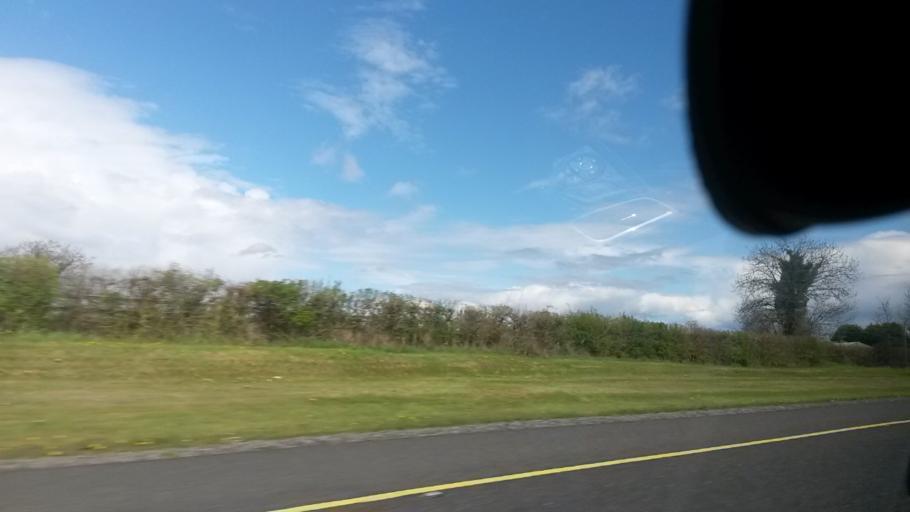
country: IE
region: Leinster
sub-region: Kildare
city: Monasterevin
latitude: 53.1118
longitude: -7.1089
